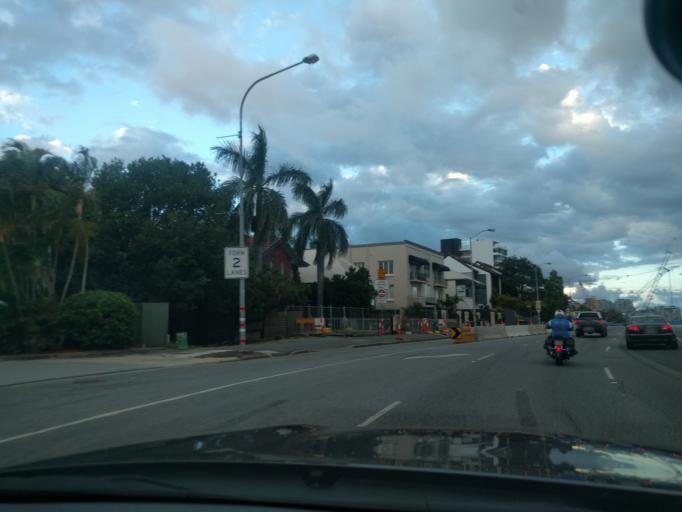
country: AU
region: Queensland
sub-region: Brisbane
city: Ascot
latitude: -27.4399
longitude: 153.0495
